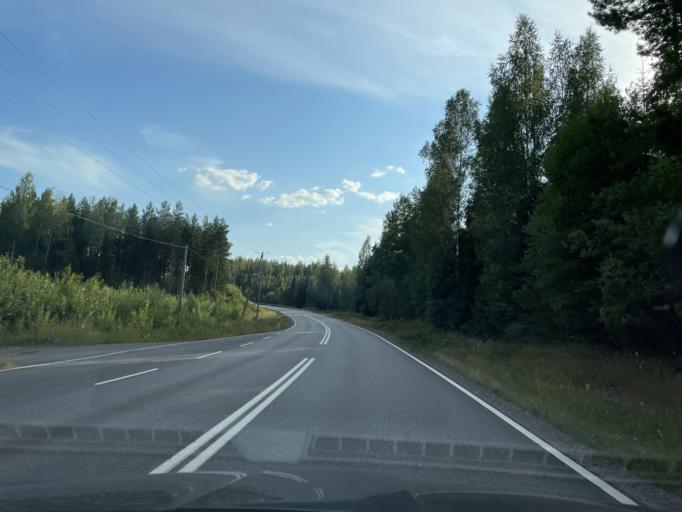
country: FI
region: Paijanne Tavastia
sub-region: Lahti
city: Auttoinen
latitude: 61.3176
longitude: 25.1330
